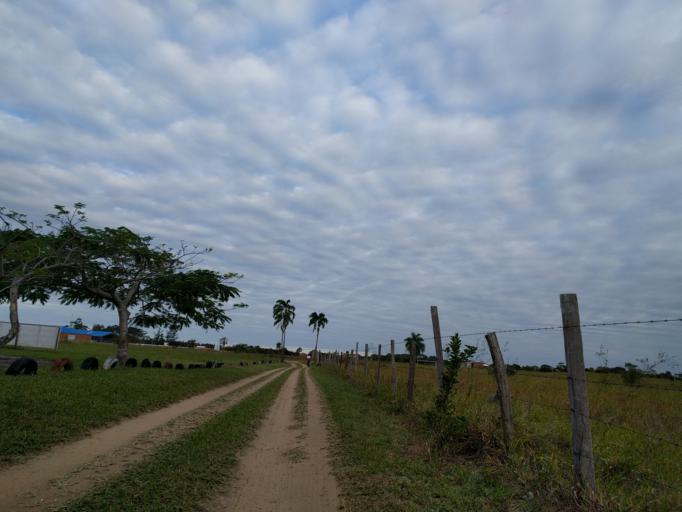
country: BO
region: Santa Cruz
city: Santa Rita
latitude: -17.8937
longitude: -63.2660
